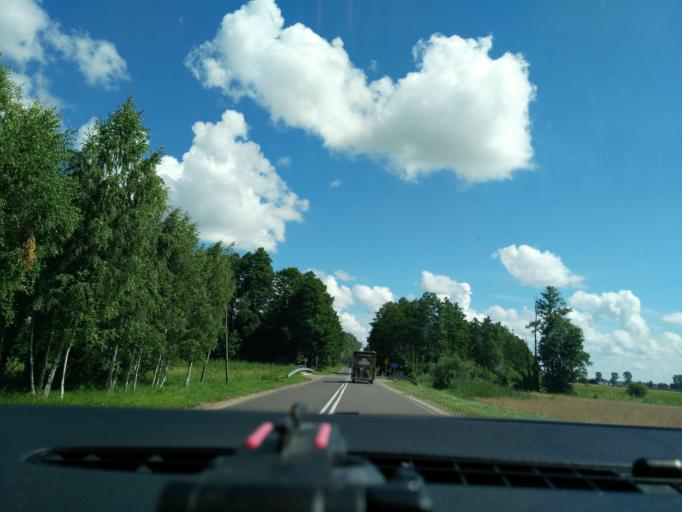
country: PL
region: Masovian Voivodeship
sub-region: Powiat losicki
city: Losice
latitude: 52.2511
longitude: 22.7920
